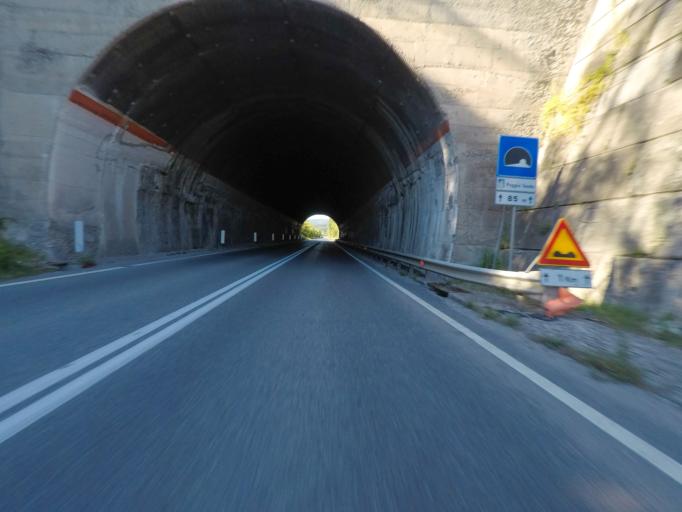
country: IT
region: Tuscany
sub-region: Provincia di Grosseto
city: Civitella Marittima
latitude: 43.0162
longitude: 11.2867
